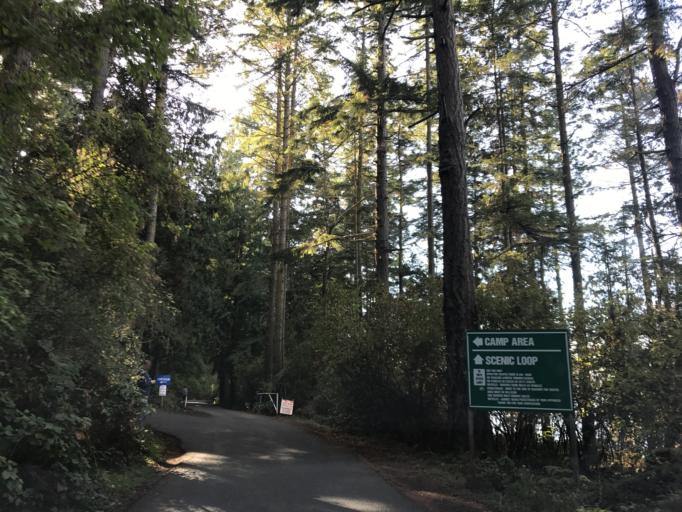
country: US
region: Washington
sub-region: Skagit County
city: Anacortes
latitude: 48.4997
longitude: -122.6940
